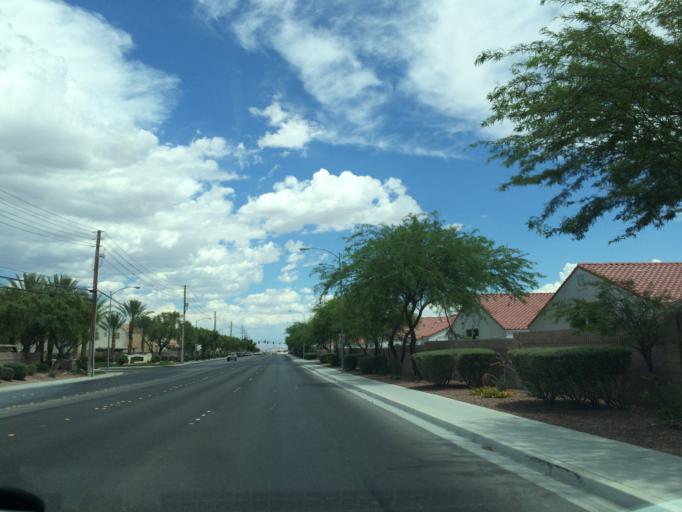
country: US
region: Nevada
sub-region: Clark County
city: North Las Vegas
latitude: 36.2467
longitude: -115.1746
